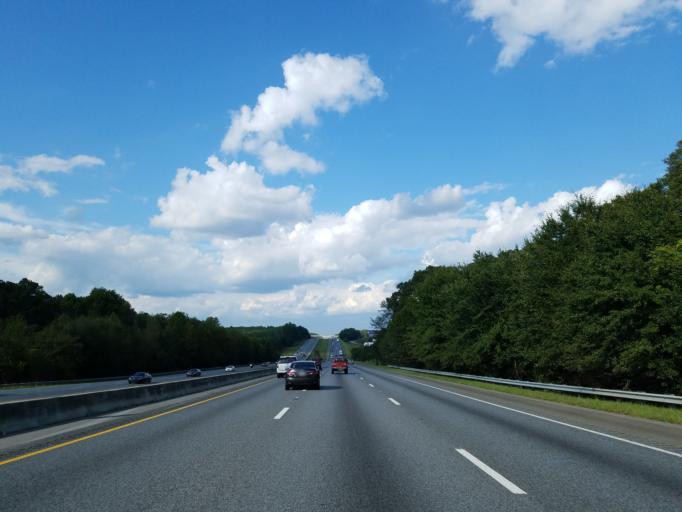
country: US
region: South Carolina
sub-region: Anderson County
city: Piedmont
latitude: 34.7312
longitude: -82.4892
